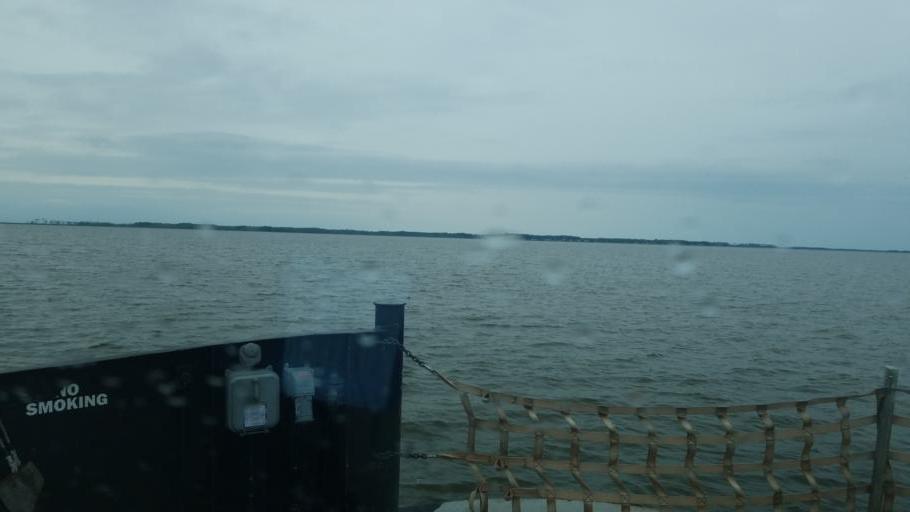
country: US
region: North Carolina
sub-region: Currituck County
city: Currituck
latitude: 36.4675
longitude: -75.9602
